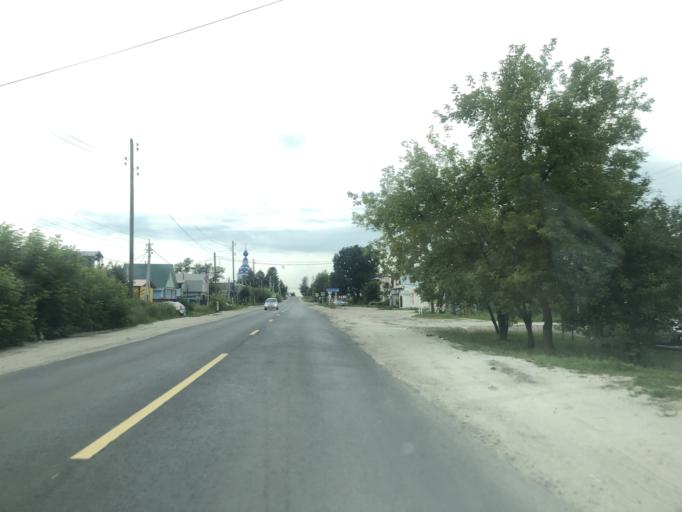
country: RU
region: Ivanovo
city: Pestyaki
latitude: 56.7060
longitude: 42.6723
